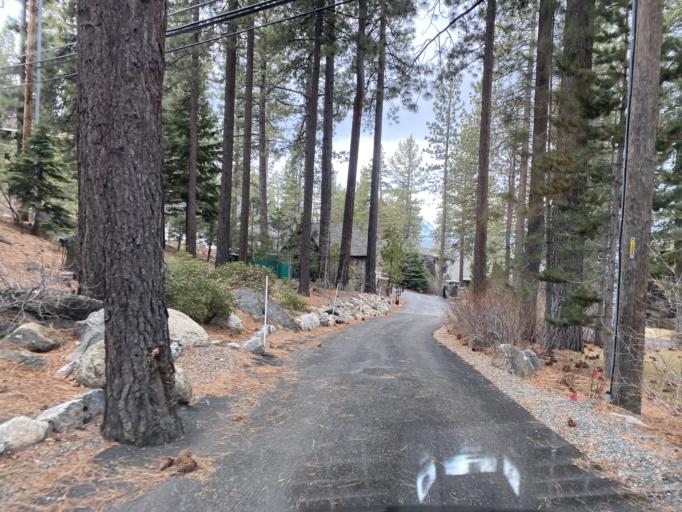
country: US
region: Nevada
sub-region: Douglas County
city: Kingsbury
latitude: 39.0277
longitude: -119.9473
